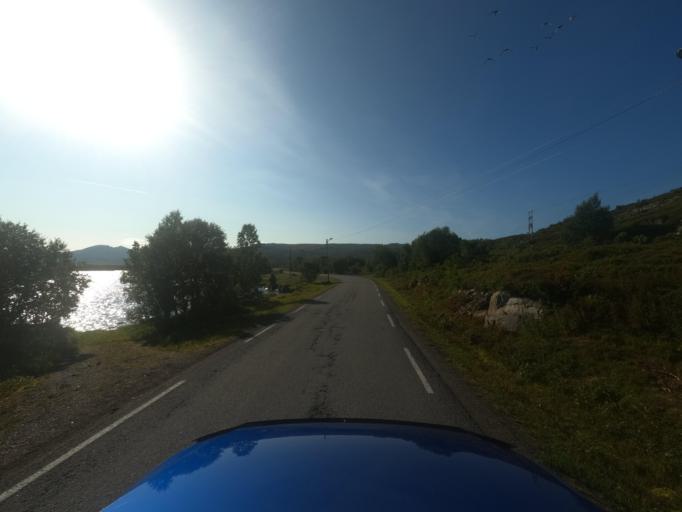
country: NO
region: Nordland
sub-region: Vestvagoy
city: Evjen
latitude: 68.3047
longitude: 13.8744
